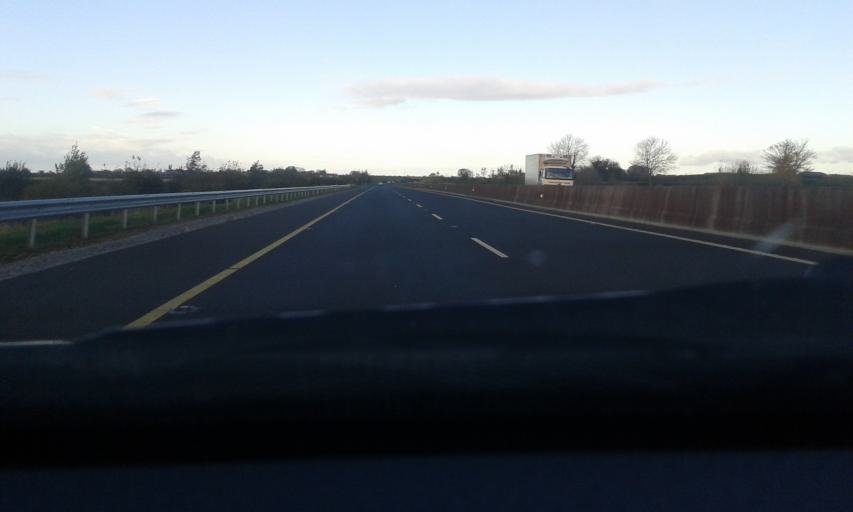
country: IE
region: Munster
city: Thurles
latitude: 52.6417
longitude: -7.7568
